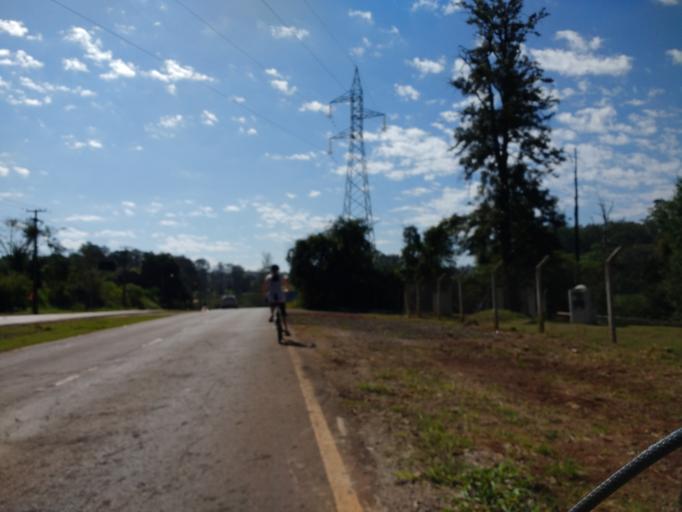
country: BR
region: Parana
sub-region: Londrina
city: Londrina
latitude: -23.3560
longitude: -51.1941
